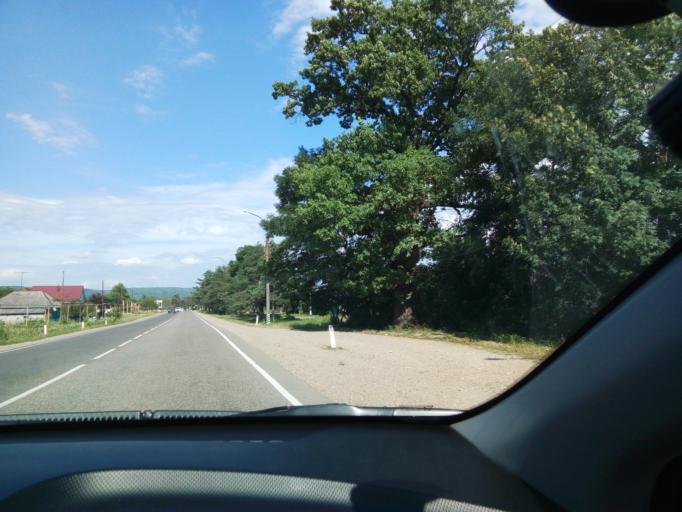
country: RU
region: Krasnodarskiy
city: Apsheronsk
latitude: 44.4635
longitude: 39.6993
